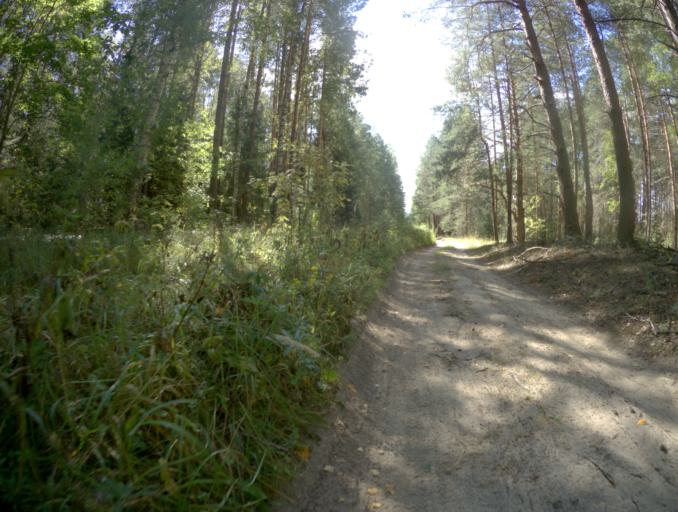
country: RU
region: Vladimir
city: Krasnaya Gorbatka
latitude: 55.8666
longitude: 41.8383
